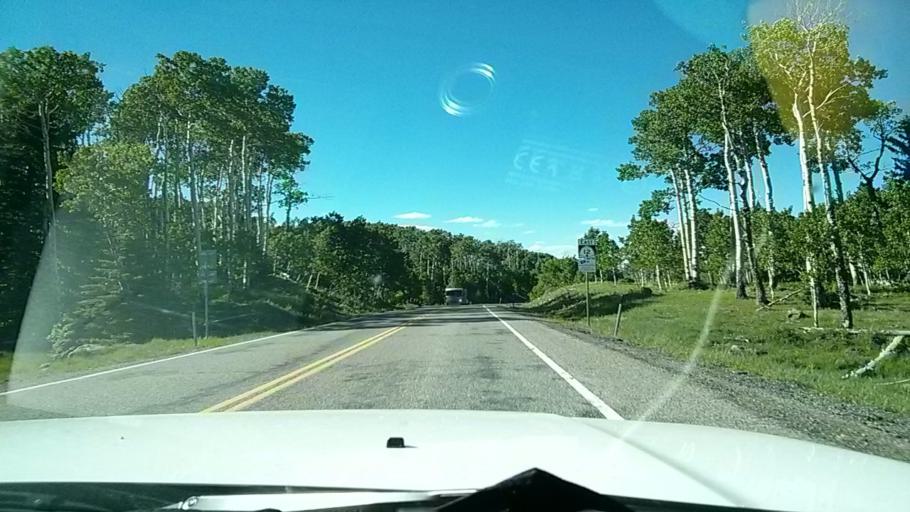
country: US
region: Utah
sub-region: Wayne County
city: Loa
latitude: 38.0636
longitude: -111.3292
